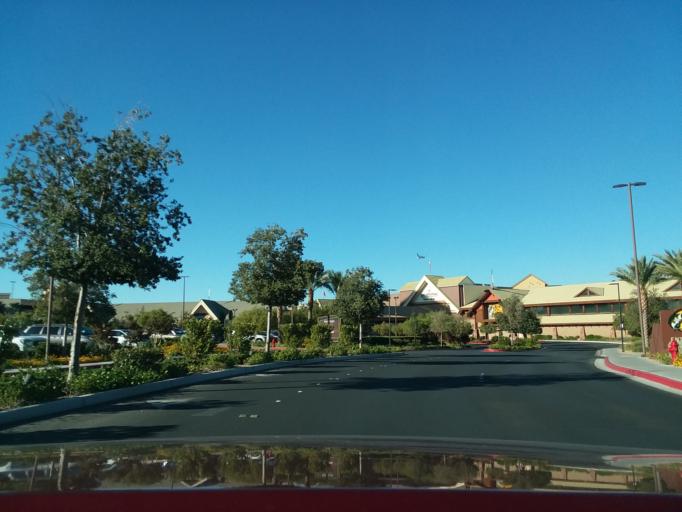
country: US
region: Nevada
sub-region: Clark County
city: Enterprise
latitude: 36.0396
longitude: -115.1835
